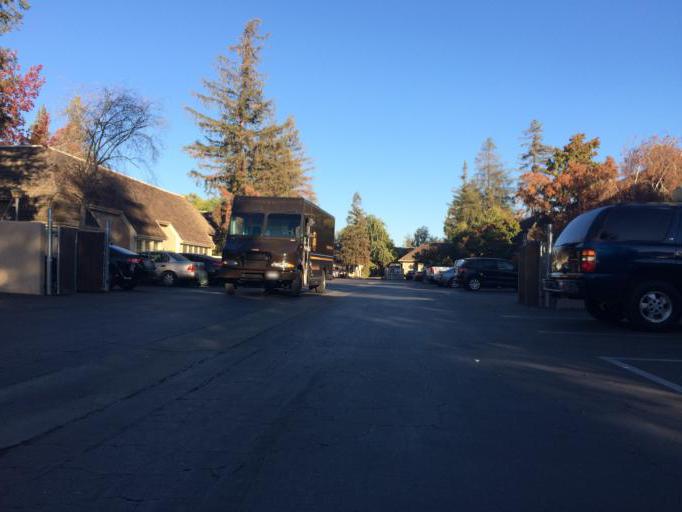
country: US
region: California
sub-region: Fresno County
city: Sunnyside
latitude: 36.7695
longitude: -119.7311
